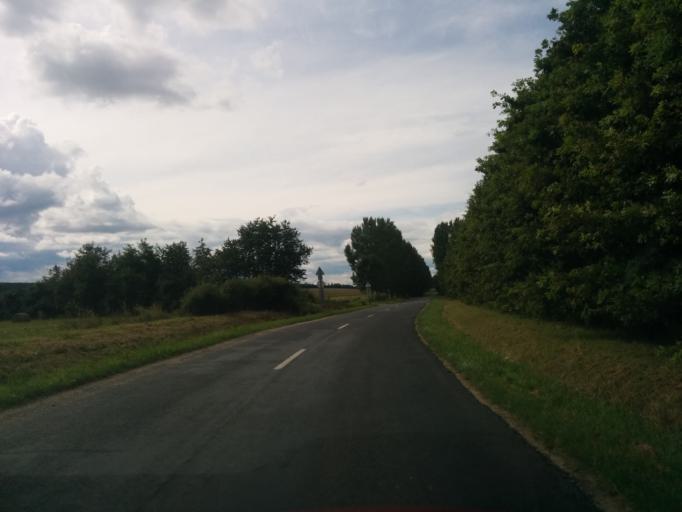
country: HU
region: Vas
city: Buk
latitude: 47.3683
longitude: 16.7365
